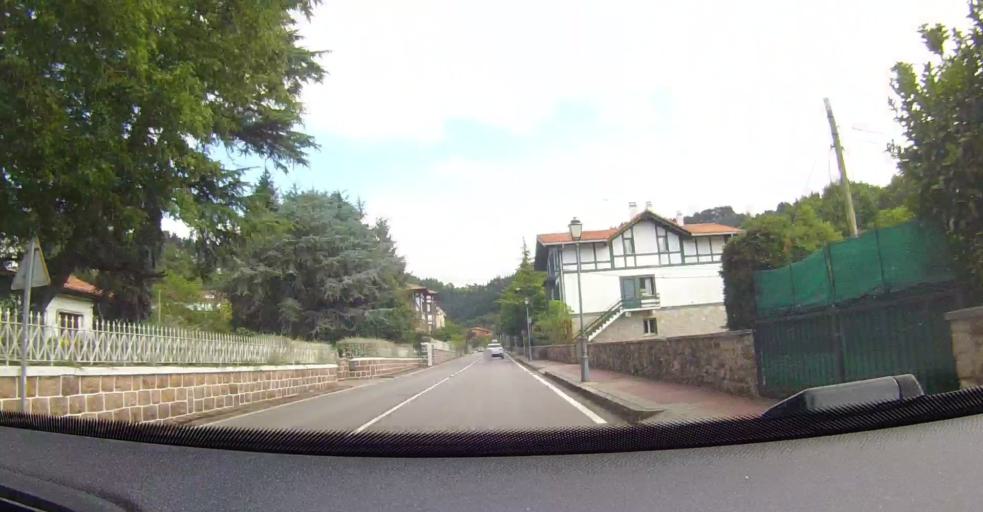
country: ES
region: Basque Country
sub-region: Bizkaia
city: Ibarrangelu
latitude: 43.3897
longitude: -2.6332
